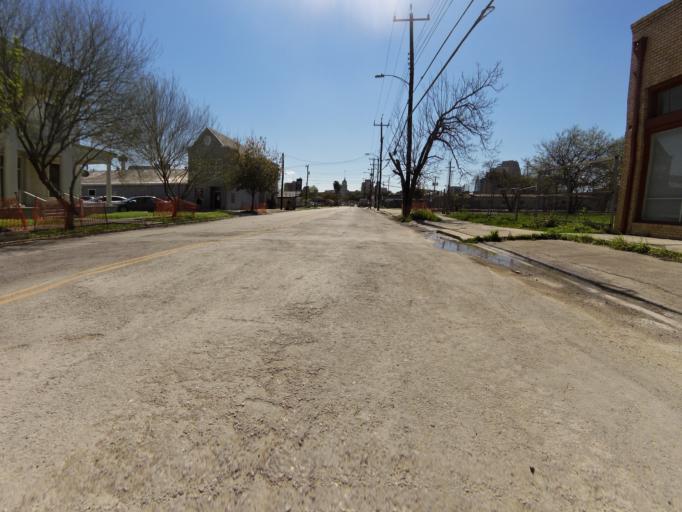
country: US
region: Texas
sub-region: Bexar County
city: San Antonio
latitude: 29.4326
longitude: -98.4810
